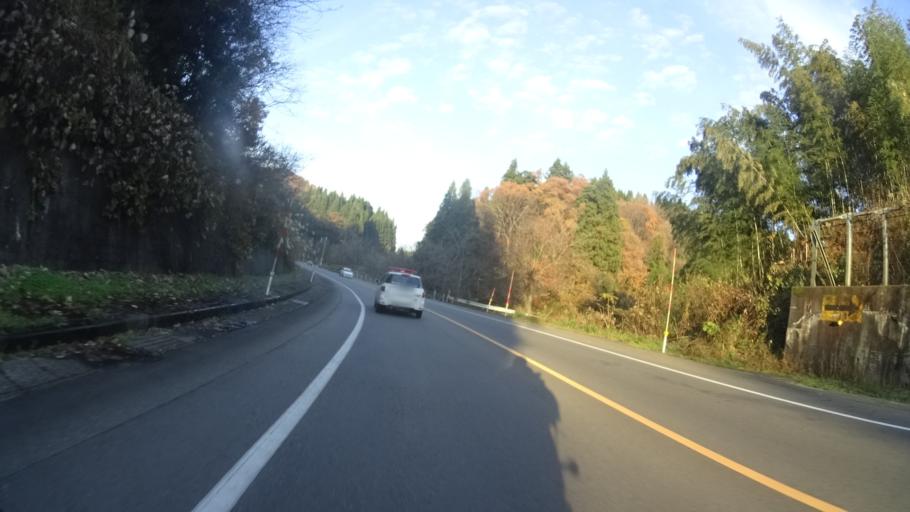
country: JP
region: Niigata
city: Ojiya
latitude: 37.4079
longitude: 138.7003
